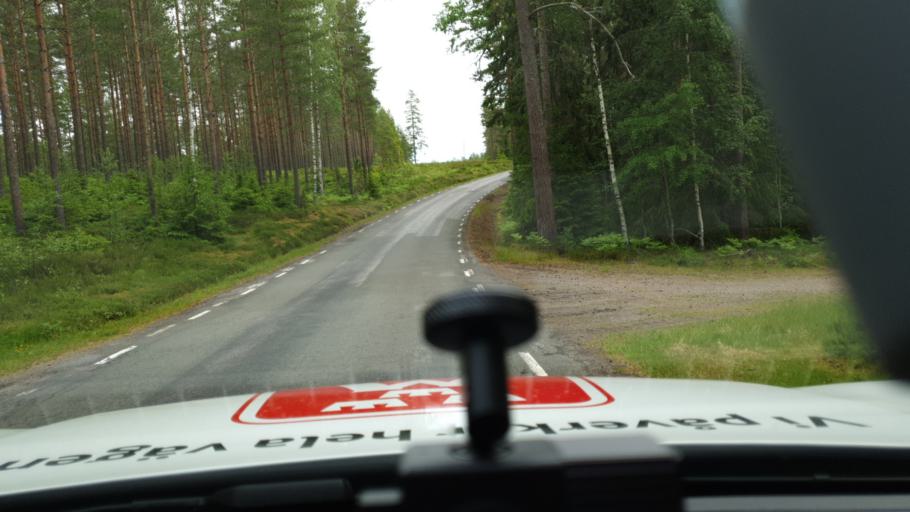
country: SE
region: Vaestra Goetaland
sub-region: Hjo Kommun
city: Hjo
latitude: 58.4107
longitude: 14.3180
